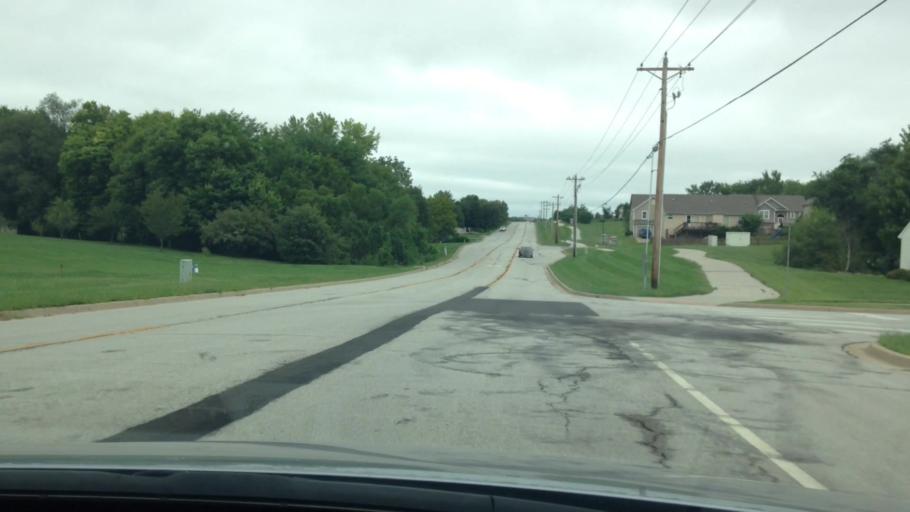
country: US
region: Missouri
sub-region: Platte County
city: Platte City
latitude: 39.3220
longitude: -94.7610
